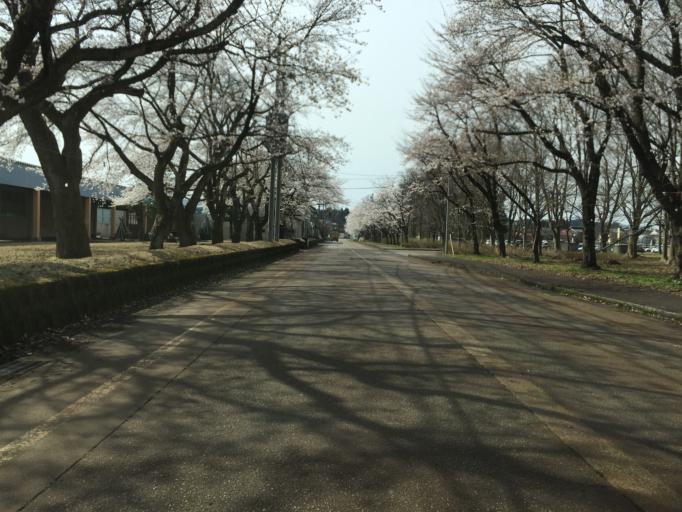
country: JP
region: Niigata
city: Ojiya
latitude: 37.3239
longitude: 138.8063
